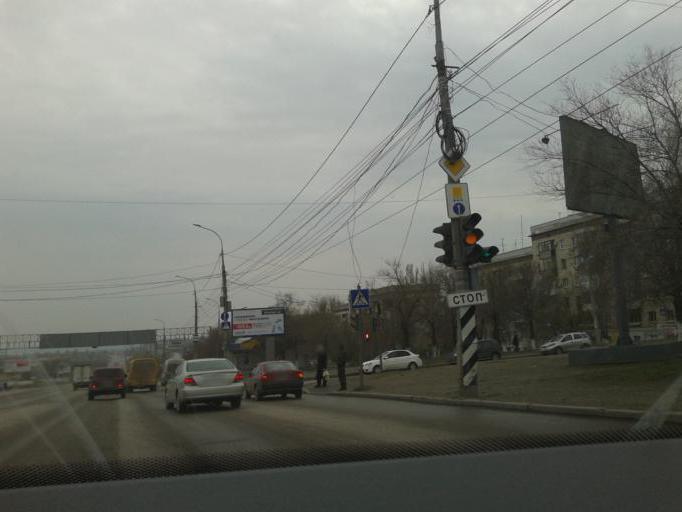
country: RU
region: Volgograd
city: Volgograd
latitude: 48.6656
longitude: 44.4405
